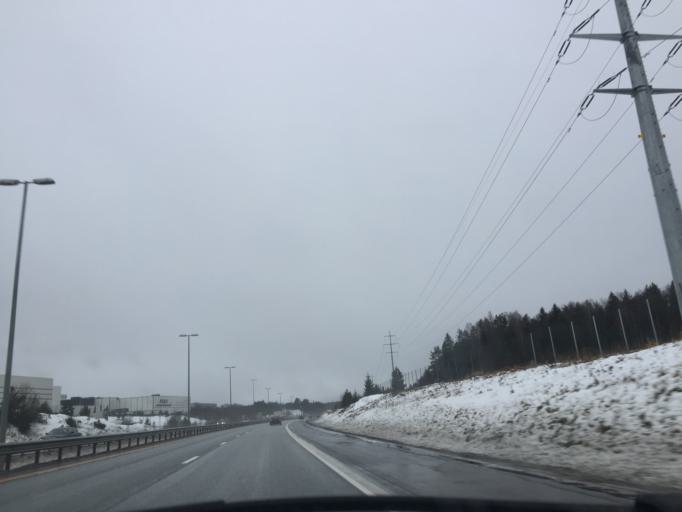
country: NO
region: Akershus
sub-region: Vestby
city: Vestby
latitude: 59.5937
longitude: 10.7385
